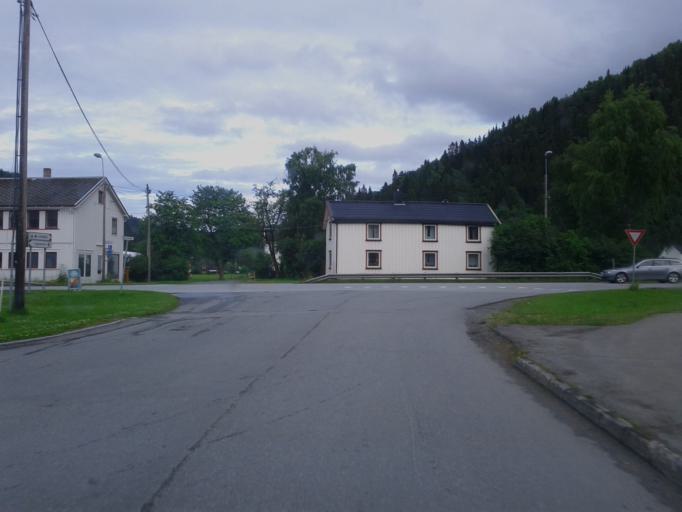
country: NO
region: Sor-Trondelag
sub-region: Melhus
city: Lundamo
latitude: 63.1535
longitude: 10.2895
